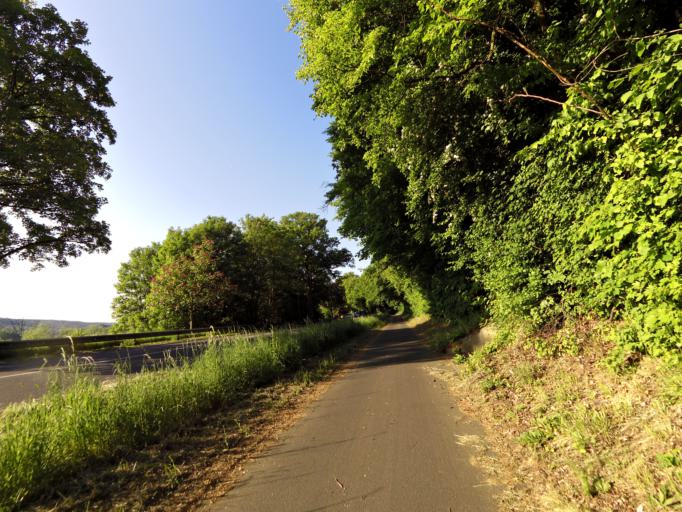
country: DE
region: North Rhine-Westphalia
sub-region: Regierungsbezirk Koln
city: Bonn
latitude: 50.6998
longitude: 7.0697
